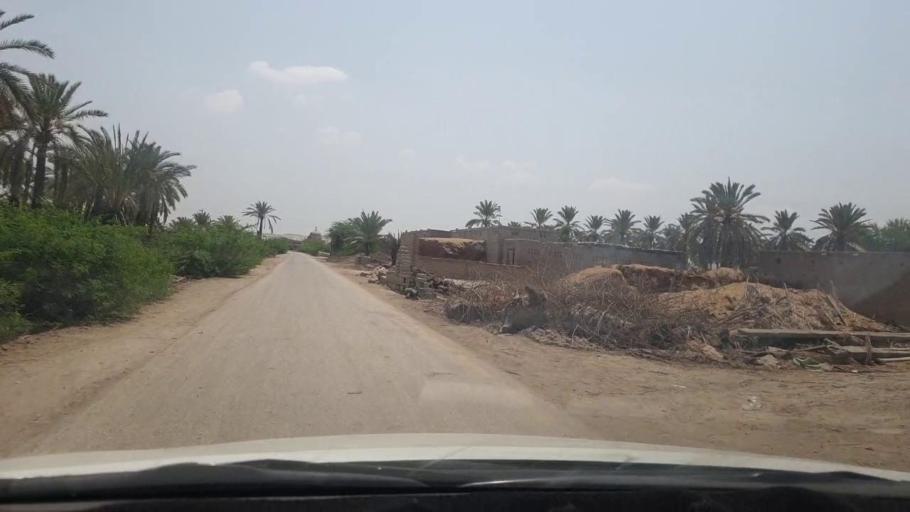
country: PK
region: Sindh
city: Khairpur
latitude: 27.5317
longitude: 68.8979
